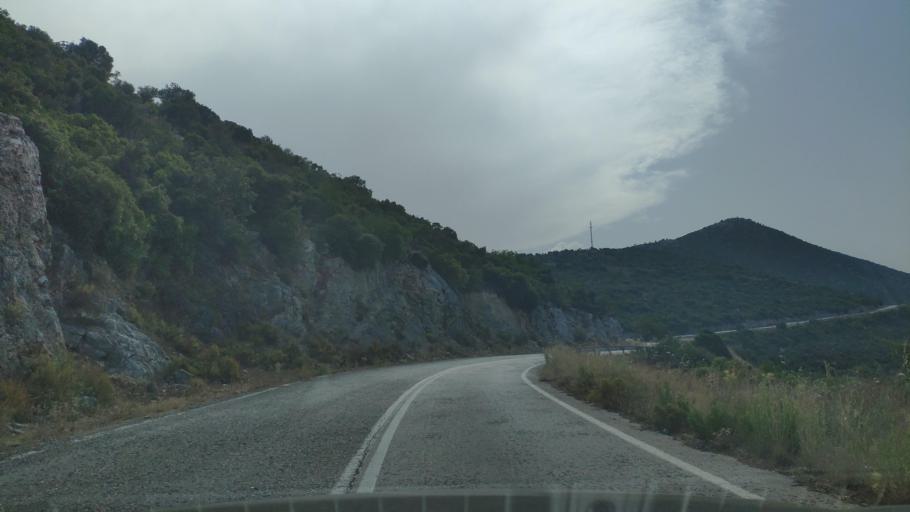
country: GR
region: Peloponnese
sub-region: Nomos Argolidos
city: Palaia Epidavros
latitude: 37.6012
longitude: 23.1630
